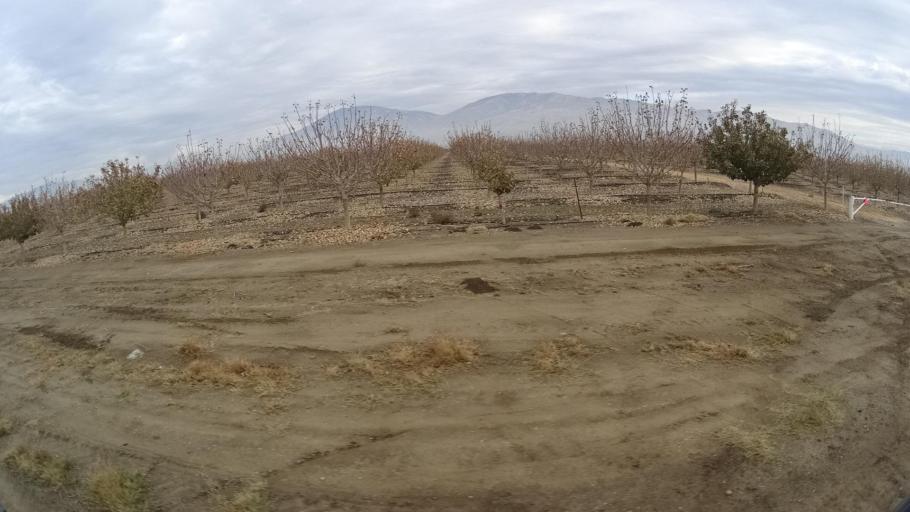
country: US
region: California
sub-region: Kern County
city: Arvin
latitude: 35.1778
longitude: -118.8239
